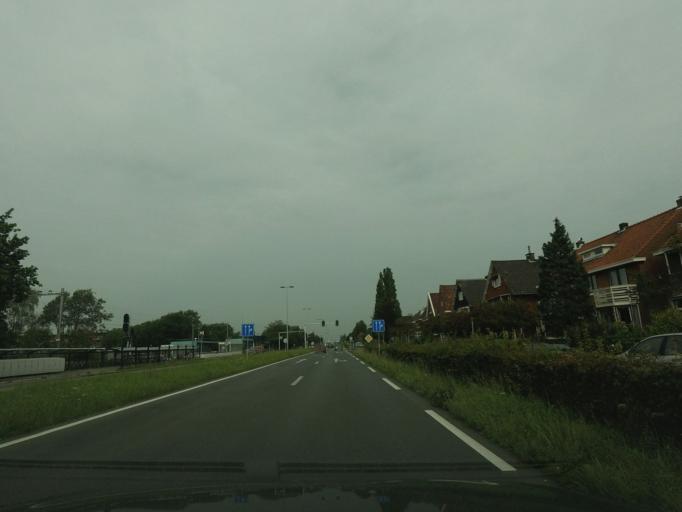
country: NL
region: North Holland
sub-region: Gemeente Zaanstad
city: Zaanstad
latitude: 52.4566
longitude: 4.8063
